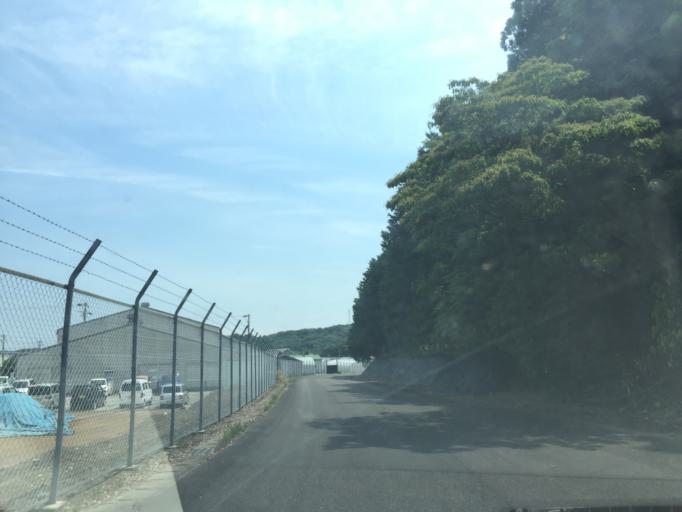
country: JP
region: Shizuoka
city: Mori
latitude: 34.8013
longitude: 137.9426
